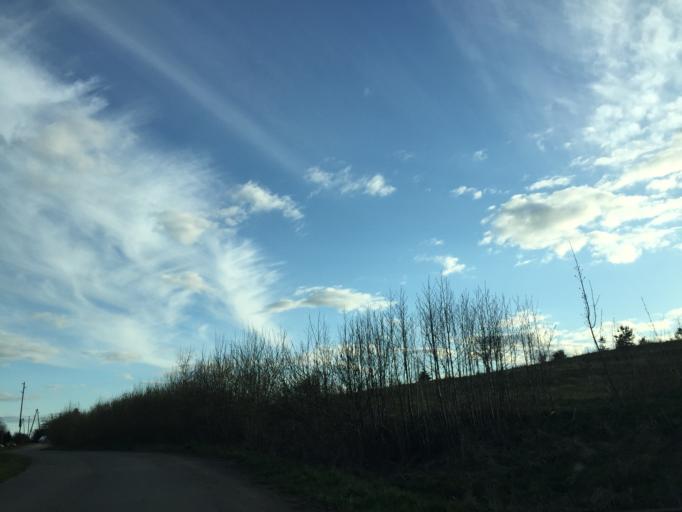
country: LV
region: Rezekne
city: Rezekne
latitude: 56.5828
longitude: 27.3372
